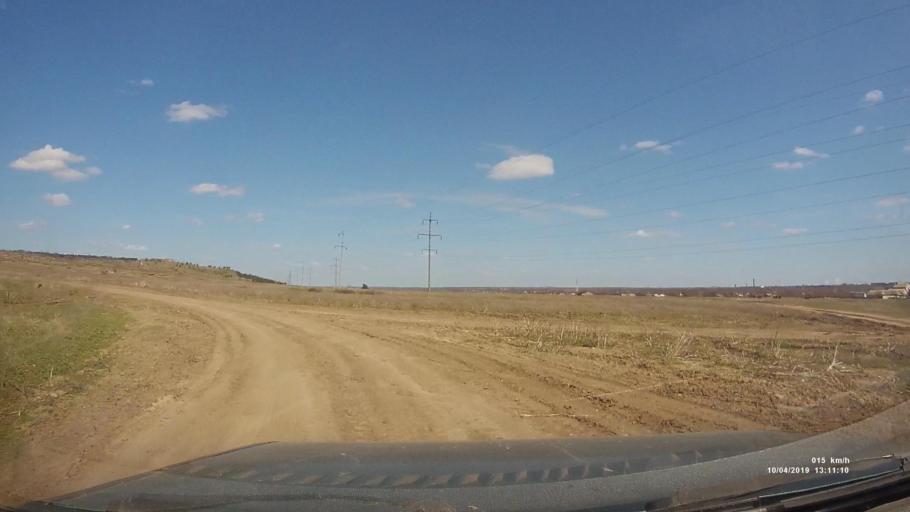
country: RU
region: Rostov
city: Masalovka
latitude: 48.4109
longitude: 40.2498
